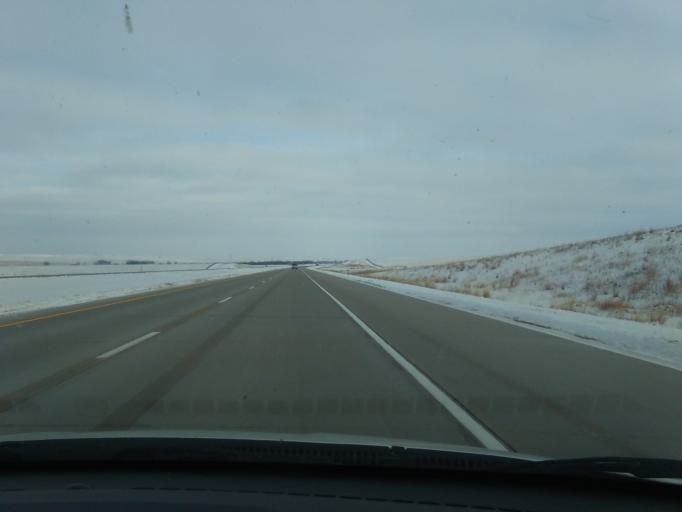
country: US
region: Nebraska
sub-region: Deuel County
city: Chappell
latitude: 41.1129
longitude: -102.5831
